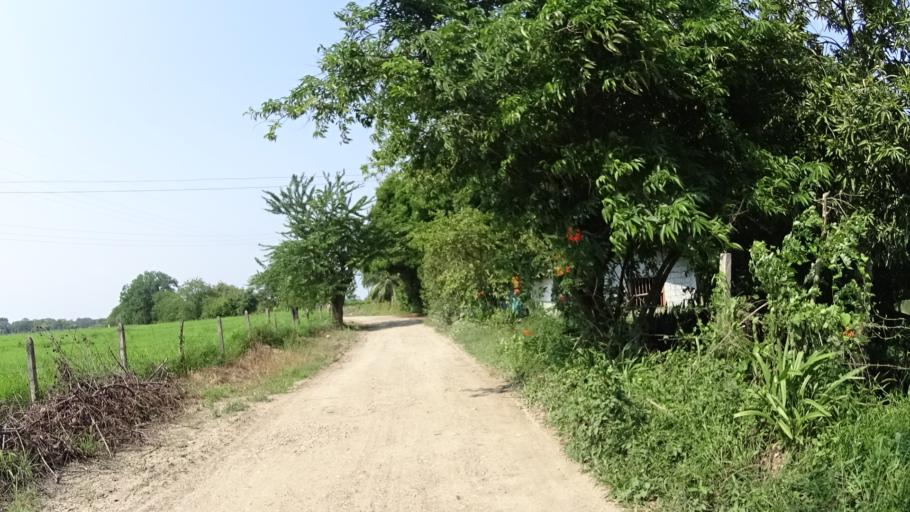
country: CO
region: Cundinamarca
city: Puerto Salgar
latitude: 5.5368
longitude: -74.6812
